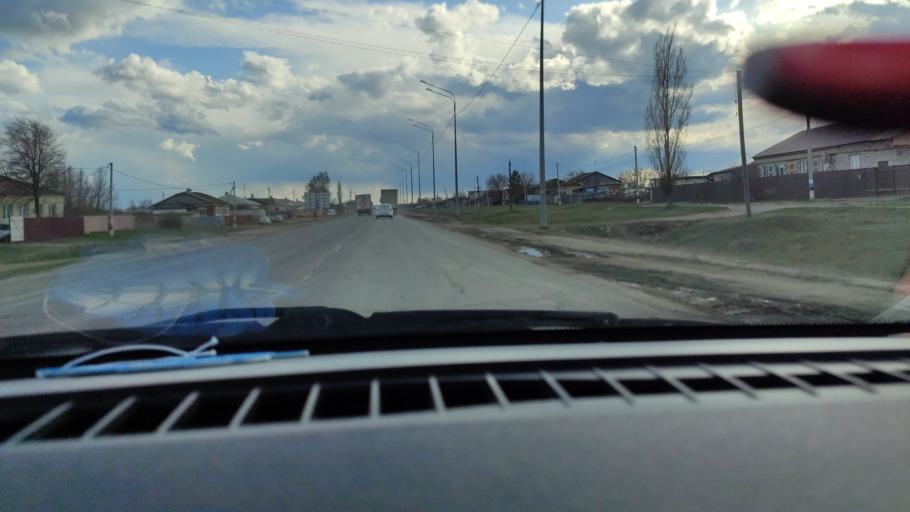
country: RU
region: Saratov
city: Sinodskoye
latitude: 51.9929
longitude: 46.6703
